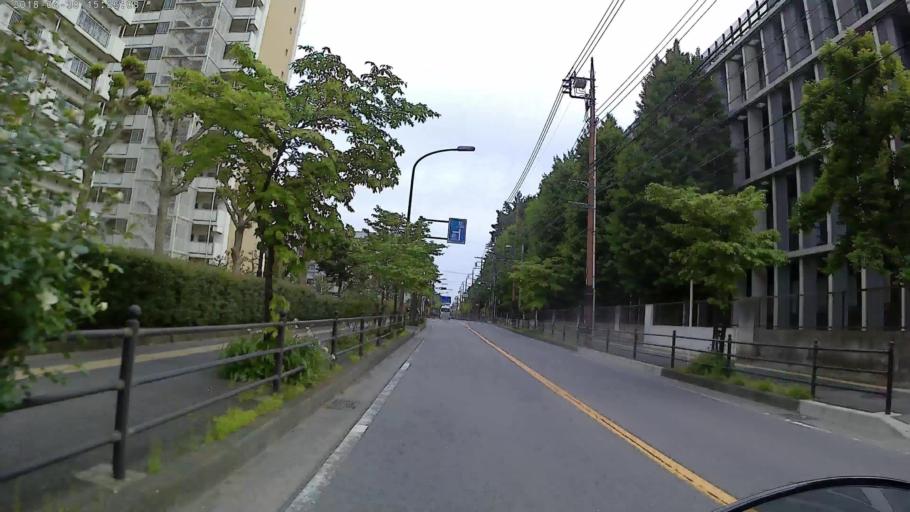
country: JP
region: Tokyo
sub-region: Machida-shi
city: Machida
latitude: 35.5344
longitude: 139.4304
